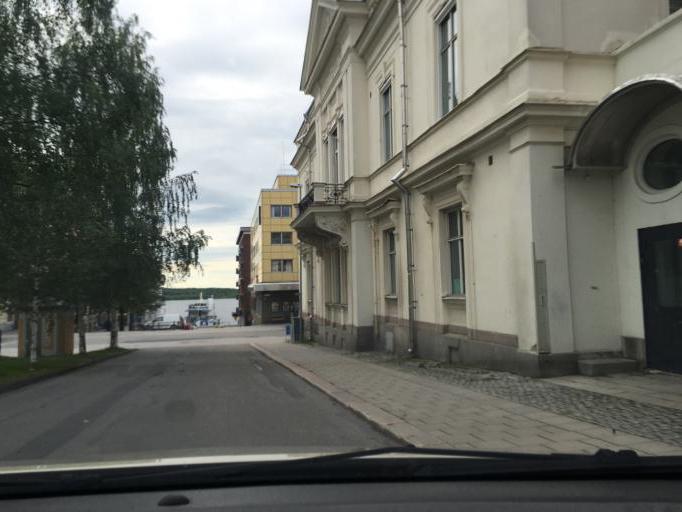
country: SE
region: Norrbotten
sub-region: Lulea Kommun
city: Lulea
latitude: 65.5832
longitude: 22.1473
